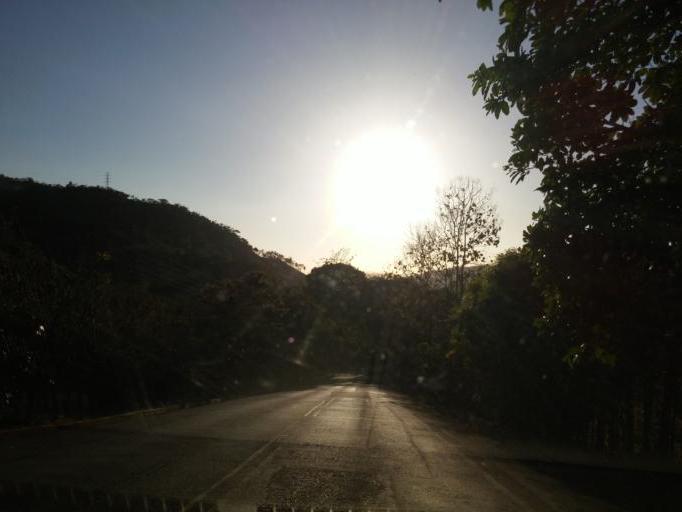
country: CR
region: Alajuela
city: Desamparados
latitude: 9.9543
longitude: -84.4873
